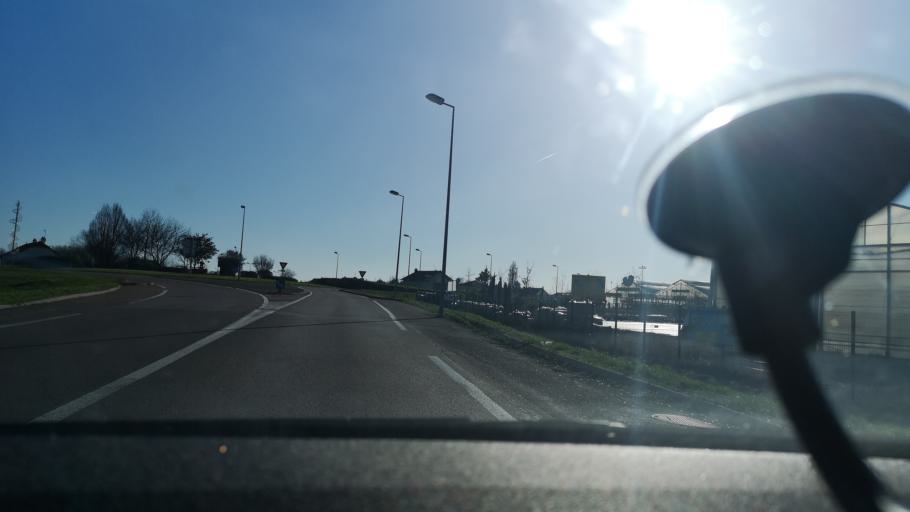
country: FR
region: Bourgogne
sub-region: Departement de Saone-et-Loire
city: Saint-Marcel
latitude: 46.7859
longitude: 4.9081
